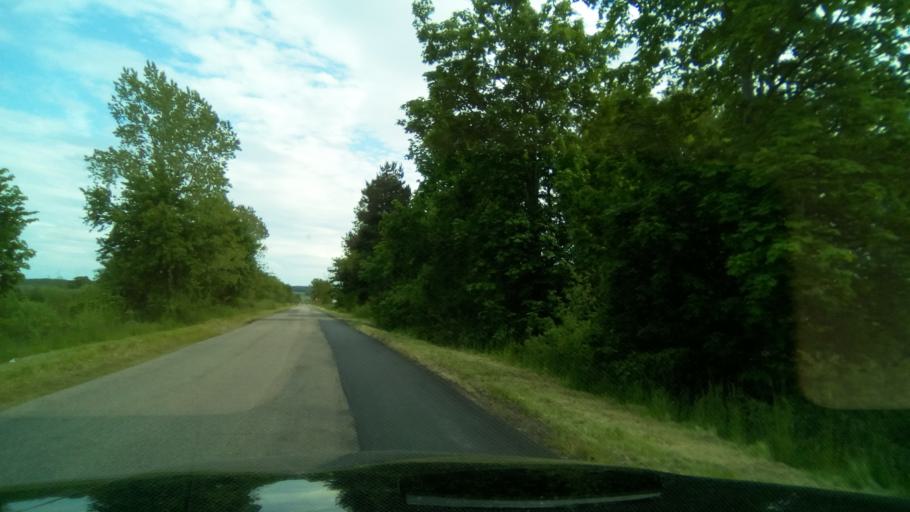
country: PL
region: Pomeranian Voivodeship
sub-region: Powiat pucki
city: Krokowa
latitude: 54.8201
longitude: 18.0869
